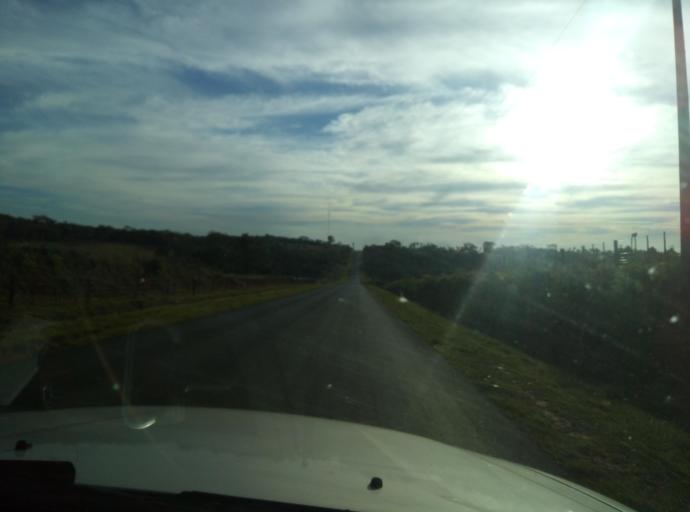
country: PY
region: Caaguazu
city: Carayao
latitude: -25.1544
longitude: -56.3171
